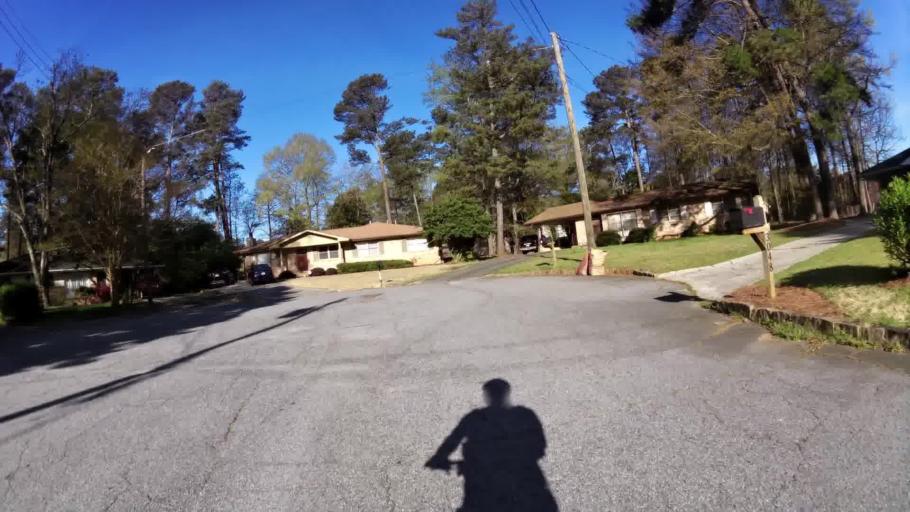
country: US
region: Georgia
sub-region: DeKalb County
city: Clarkston
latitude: 33.8381
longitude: -84.2641
